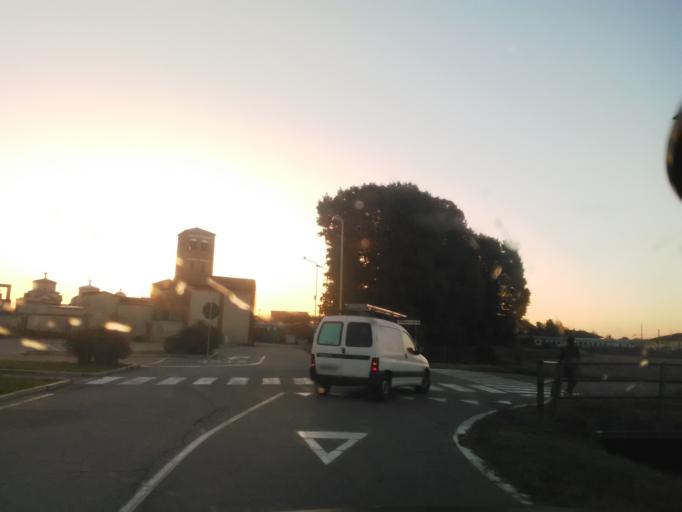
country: IT
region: Piedmont
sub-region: Provincia di Vercelli
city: Tronzano Vercellese
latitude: 45.3470
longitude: 8.1686
